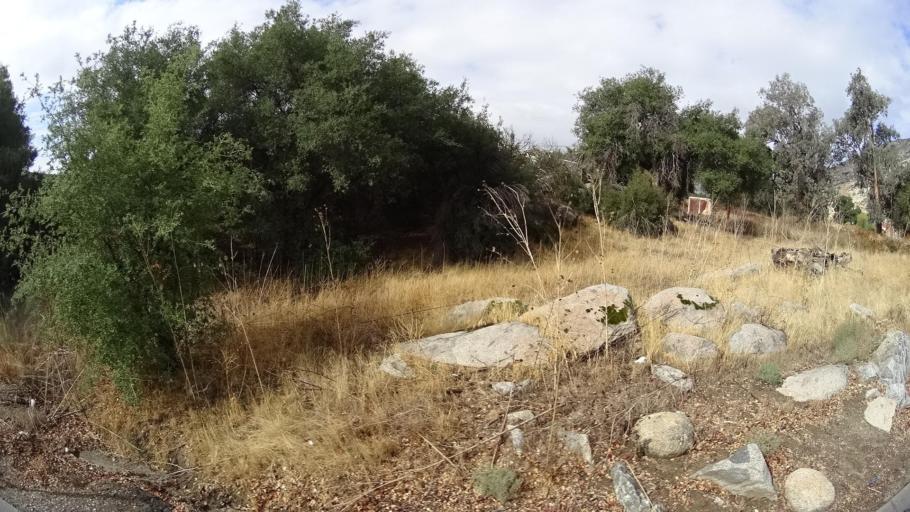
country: MX
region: Baja California
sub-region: Tecate
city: Hacienda Tecate
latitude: 32.5947
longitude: -116.5279
